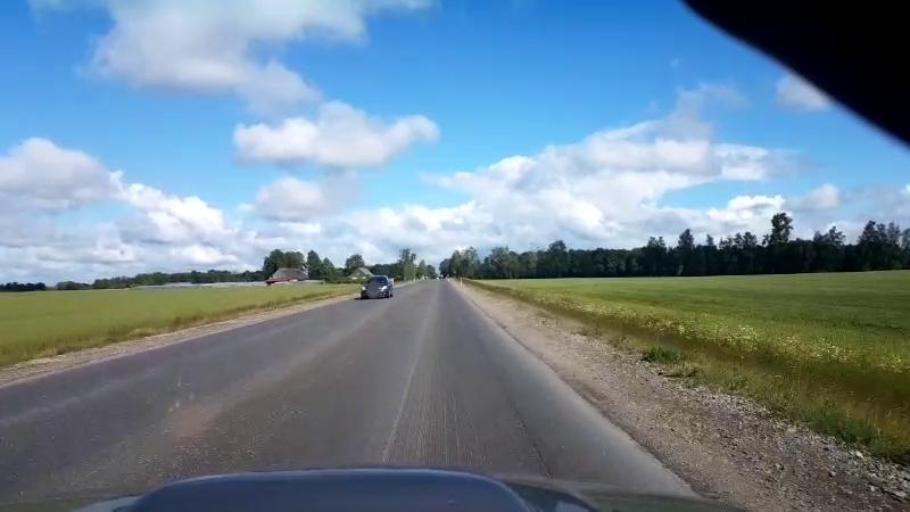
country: LV
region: Bauskas Rajons
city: Bauska
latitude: 56.3758
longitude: 24.2664
